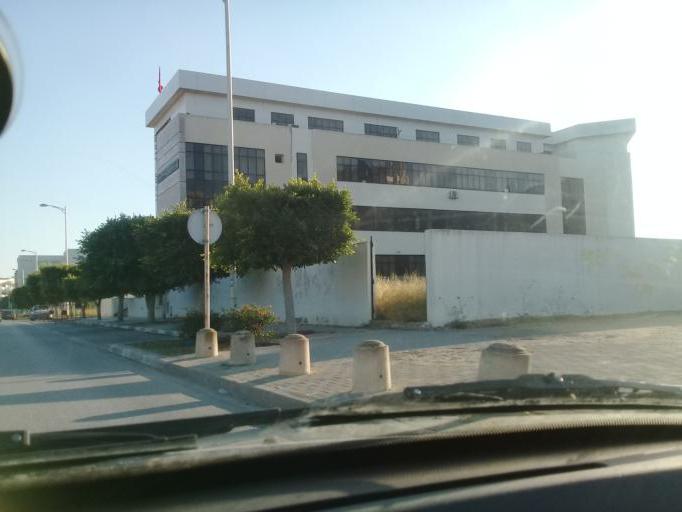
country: TN
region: Tunis
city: La Goulette
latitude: 36.8461
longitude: 10.2783
